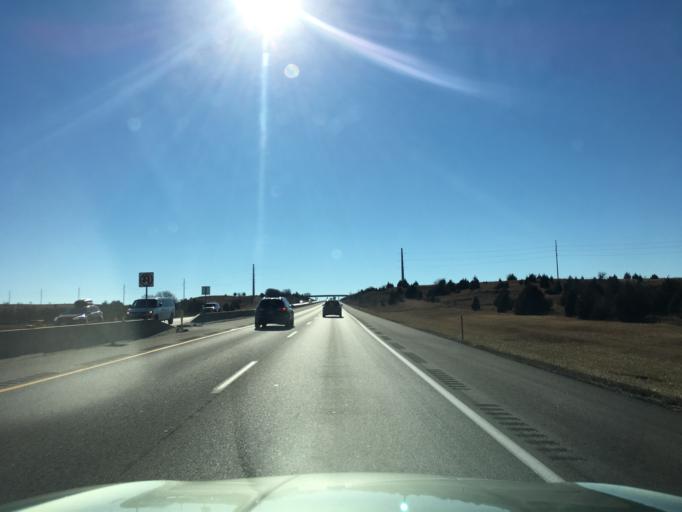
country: US
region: Kansas
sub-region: Sumner County
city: Wellington
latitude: 37.2098
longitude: -97.3400
